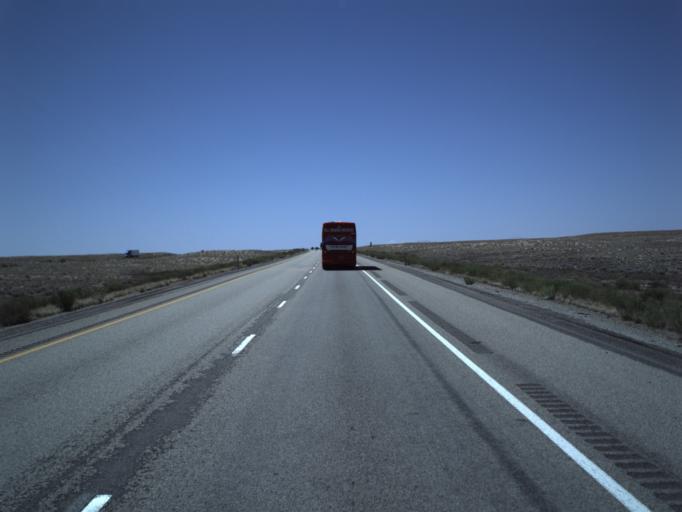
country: US
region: Utah
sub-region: Grand County
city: Moab
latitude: 38.9635
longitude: -109.3768
